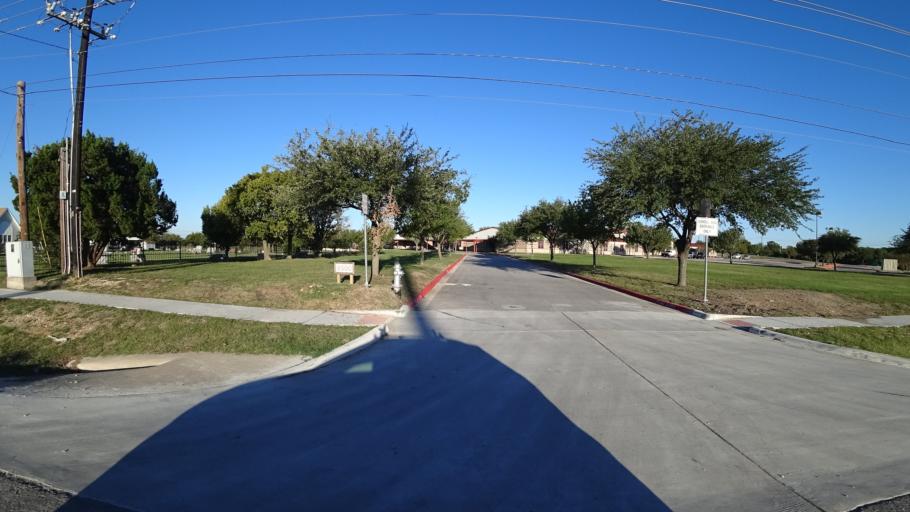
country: US
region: Texas
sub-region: Travis County
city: Manor
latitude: 30.3105
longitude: -97.6157
